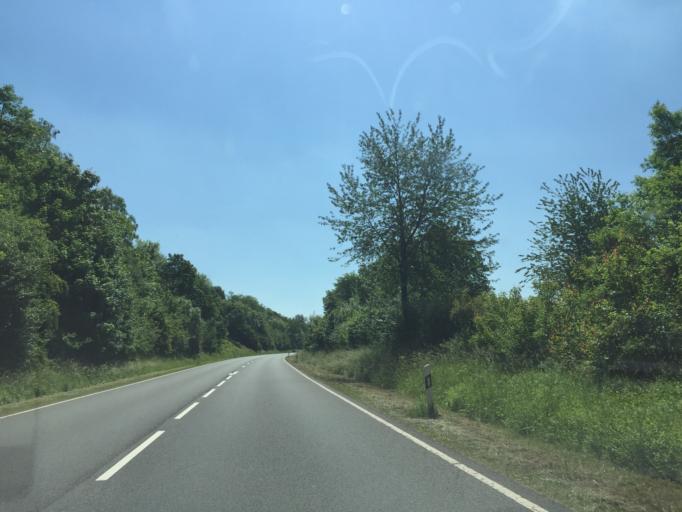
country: DE
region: Baden-Wuerttemberg
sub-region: Karlsruhe Region
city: Walldurn
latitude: 49.5908
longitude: 9.3634
